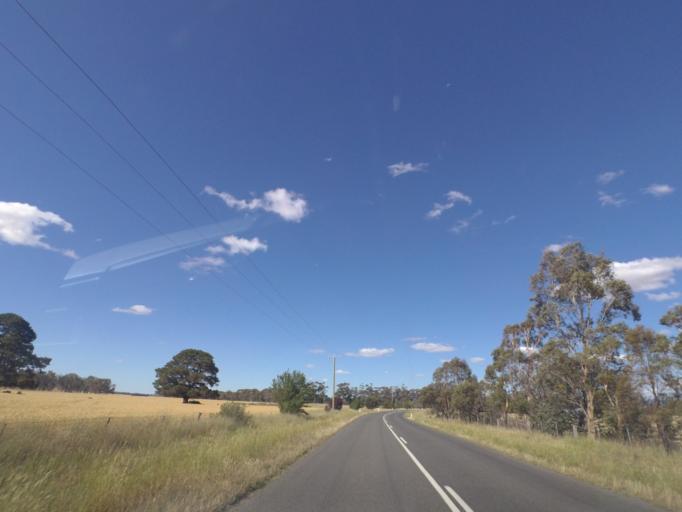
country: AU
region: Victoria
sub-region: Hume
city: Sunbury
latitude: -37.4270
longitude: 144.8533
